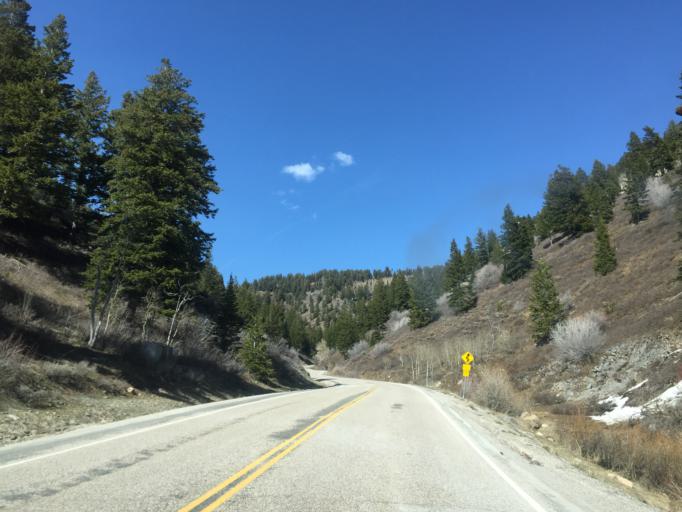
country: US
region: Utah
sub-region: Weber County
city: Wolf Creek
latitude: 41.3646
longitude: -111.7839
